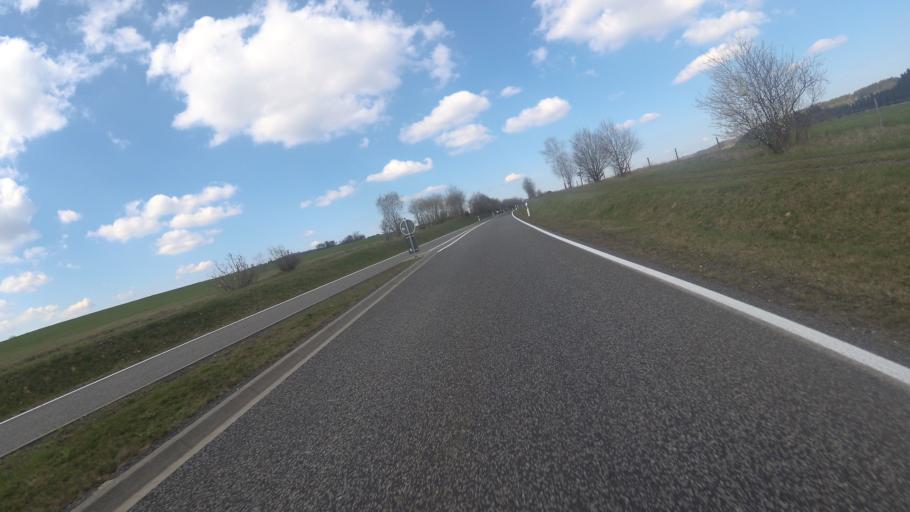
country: DE
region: Rheinland-Pfalz
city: Kradenbach
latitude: 50.2375
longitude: 6.8530
